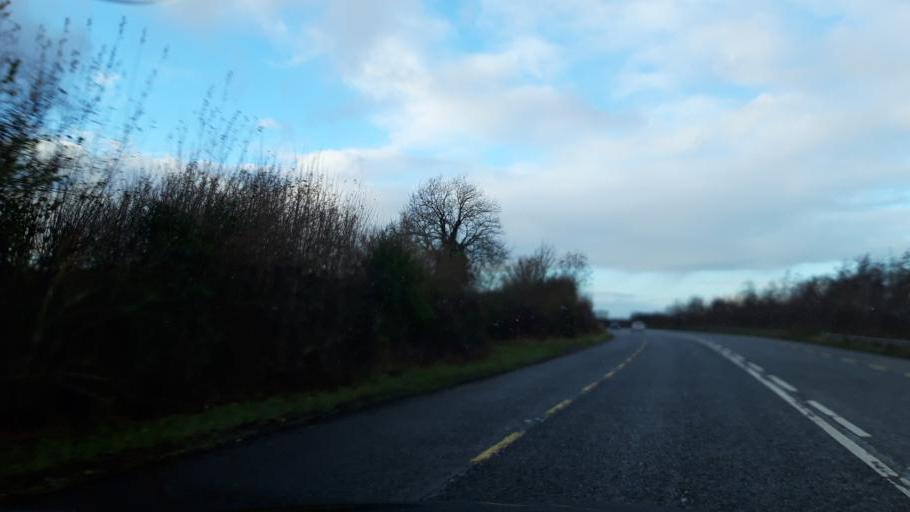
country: IE
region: Ulster
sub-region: County Monaghan
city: Carrickmacross
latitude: 53.9212
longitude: -6.6325
